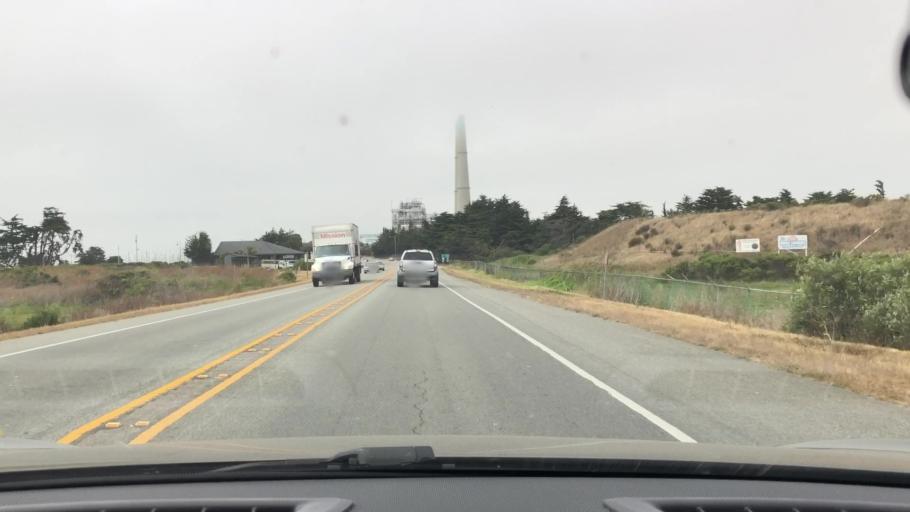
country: US
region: California
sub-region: Monterey County
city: Castroville
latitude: 36.7969
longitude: -121.7826
